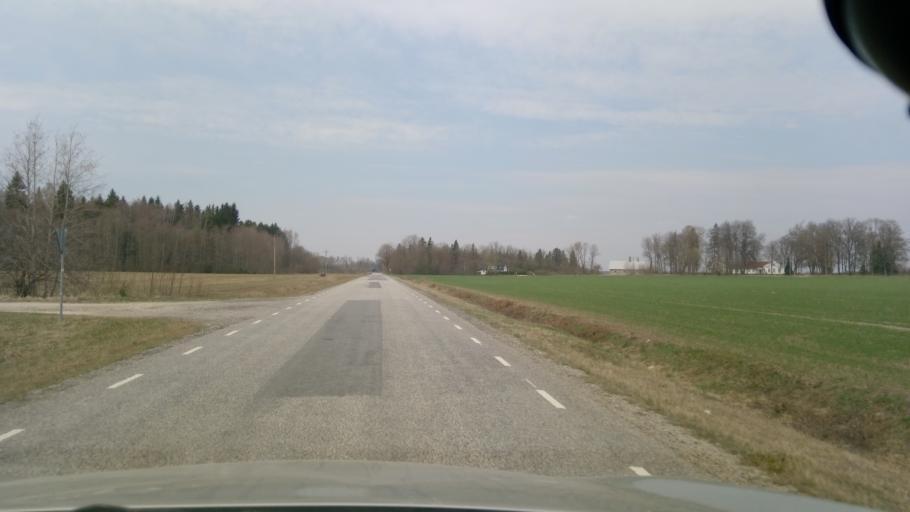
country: EE
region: Jaervamaa
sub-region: Tueri vald
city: Tueri
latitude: 58.8007
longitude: 25.4754
